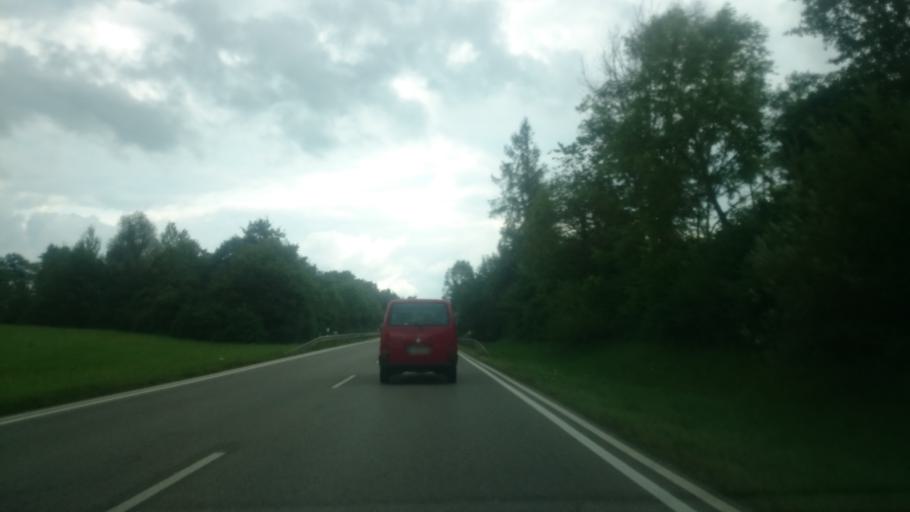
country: DE
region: Bavaria
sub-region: Swabia
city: Mauerstetten
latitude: 47.8723
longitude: 10.6492
